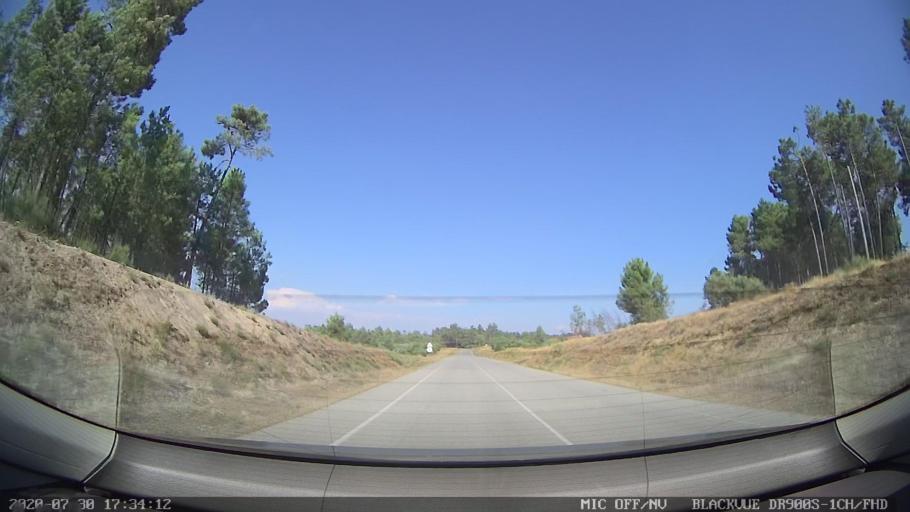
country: PT
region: Vila Real
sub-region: Murca
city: Murca
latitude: 41.3530
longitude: -7.4825
